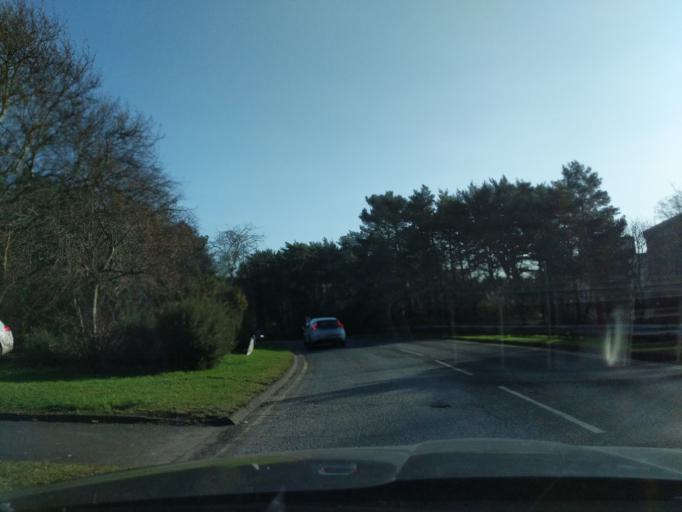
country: GB
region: England
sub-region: Sunderland
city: Washington
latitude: 54.8977
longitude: -1.5348
